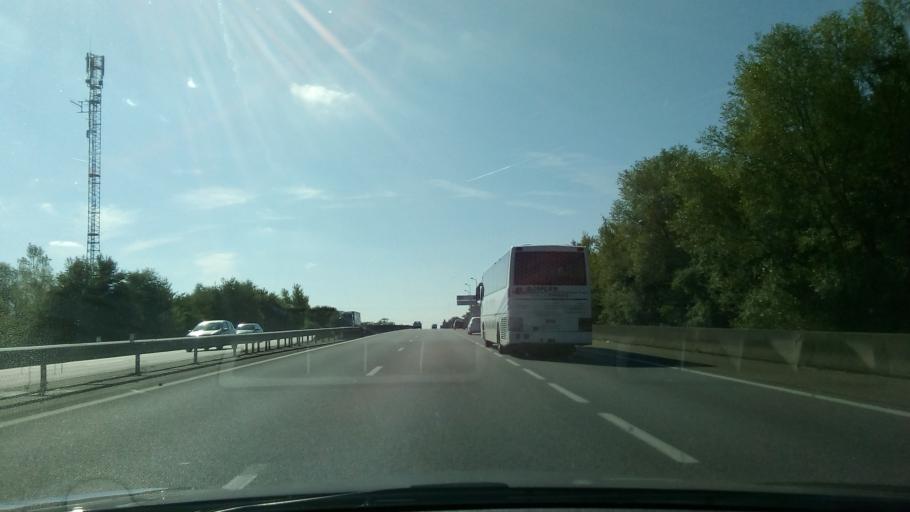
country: FR
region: Ile-de-France
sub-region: Departement de Seine-et-Marne
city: Nandy
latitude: 48.6099
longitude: 2.5755
